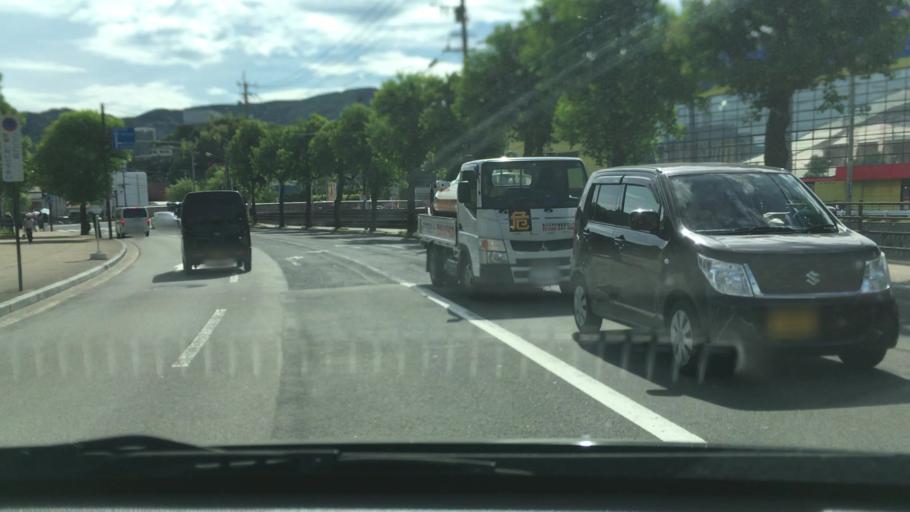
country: JP
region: Nagasaki
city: Nagasaki-shi
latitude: 32.7780
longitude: 129.8609
